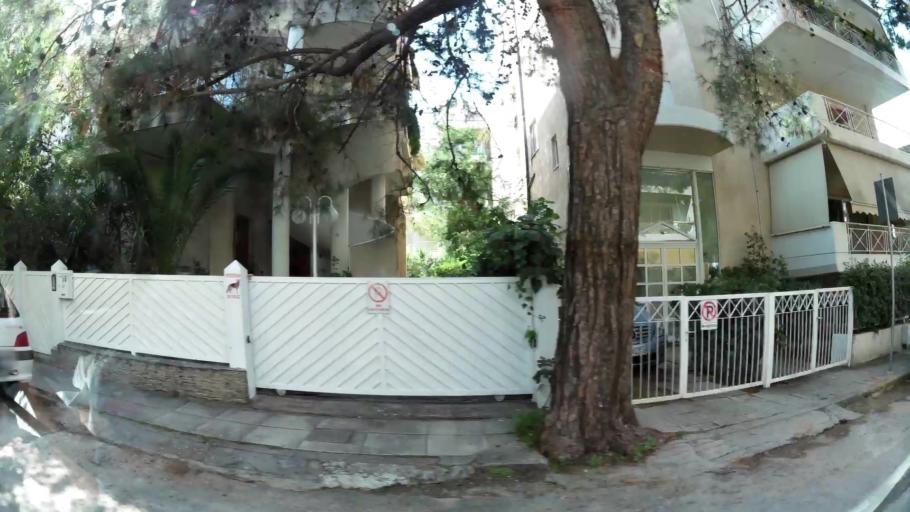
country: GR
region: Attica
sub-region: Nomarchia Athinas
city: Cholargos
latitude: 37.9981
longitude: 23.7948
